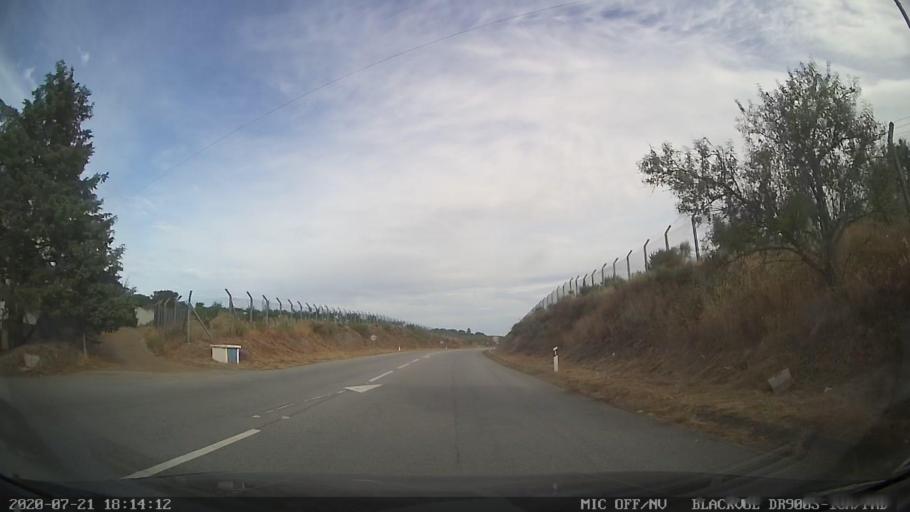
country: PT
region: Viseu
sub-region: Sao Joao da Pesqueira
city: Sao Joao da Pesqueira
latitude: 41.1255
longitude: -7.3922
